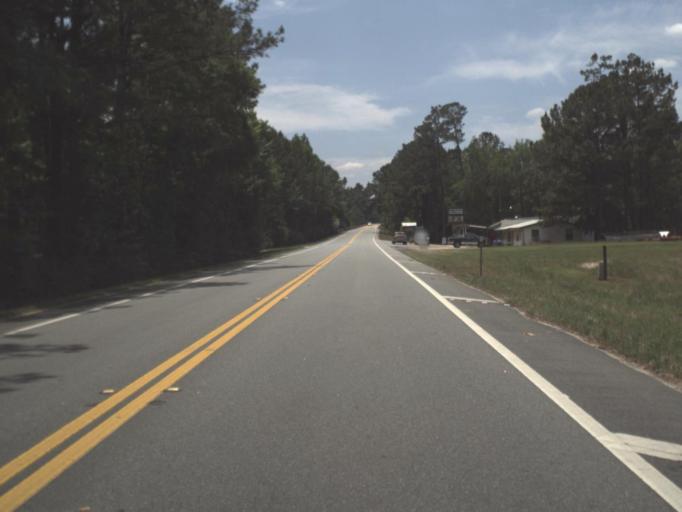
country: US
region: Florida
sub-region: Calhoun County
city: Blountstown
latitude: 30.2895
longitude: -85.1410
